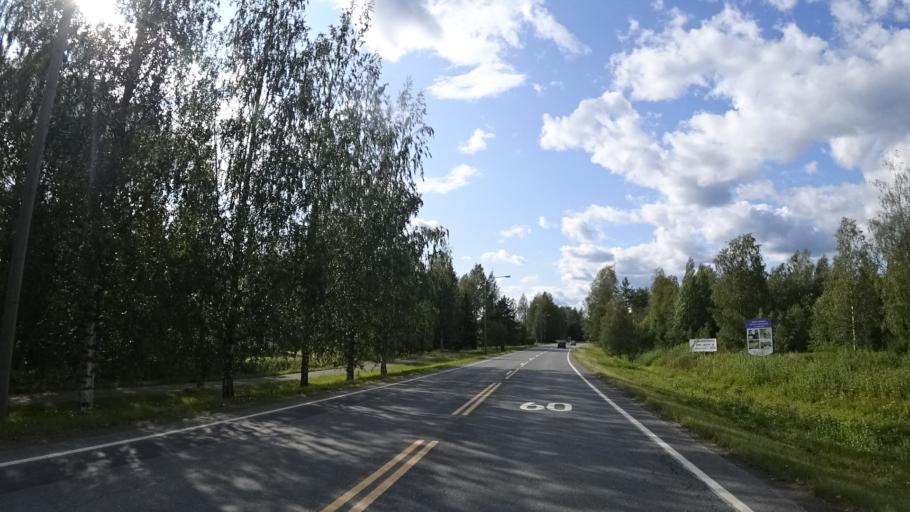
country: FI
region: North Karelia
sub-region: Keski-Karjala
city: Tohmajaervi
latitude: 62.2230
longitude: 30.3447
